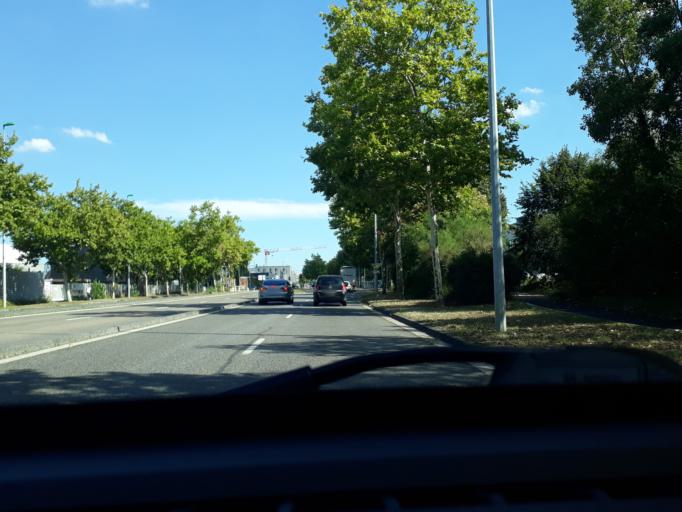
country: FR
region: Rhone-Alpes
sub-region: Departement du Rhone
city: Saint-Priest
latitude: 45.7028
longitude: 4.9156
